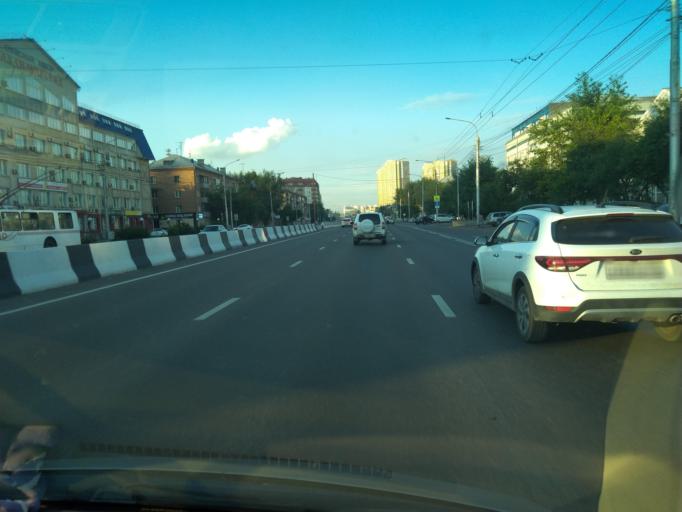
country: RU
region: Krasnoyarskiy
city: Krasnoyarsk
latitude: 56.0286
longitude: 92.9130
